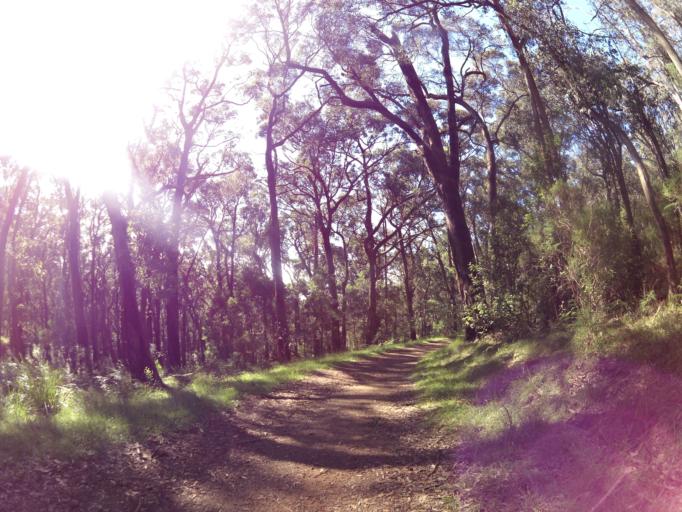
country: AU
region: Victoria
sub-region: Knox
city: The Basin
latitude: -37.8706
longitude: 145.3157
